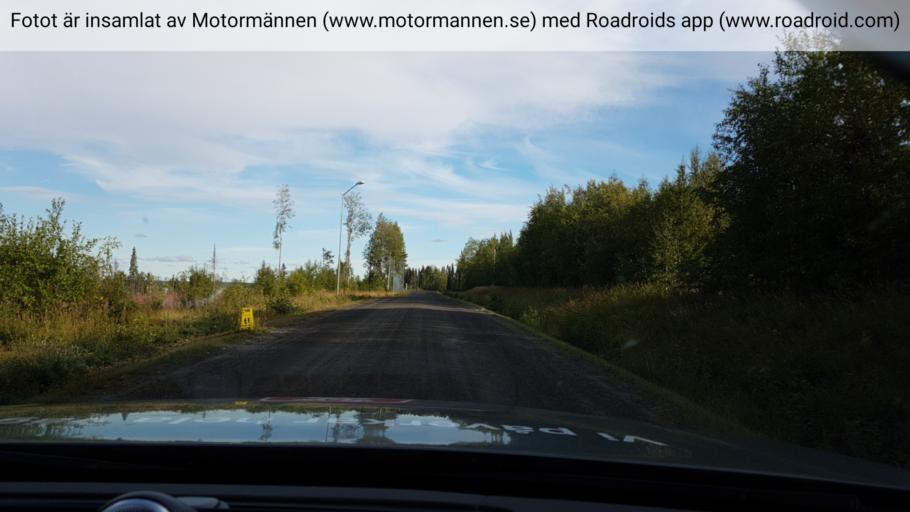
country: SE
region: Jaemtland
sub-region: Stroemsunds Kommun
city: Stroemsund
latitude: 64.1243
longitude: 15.8016
